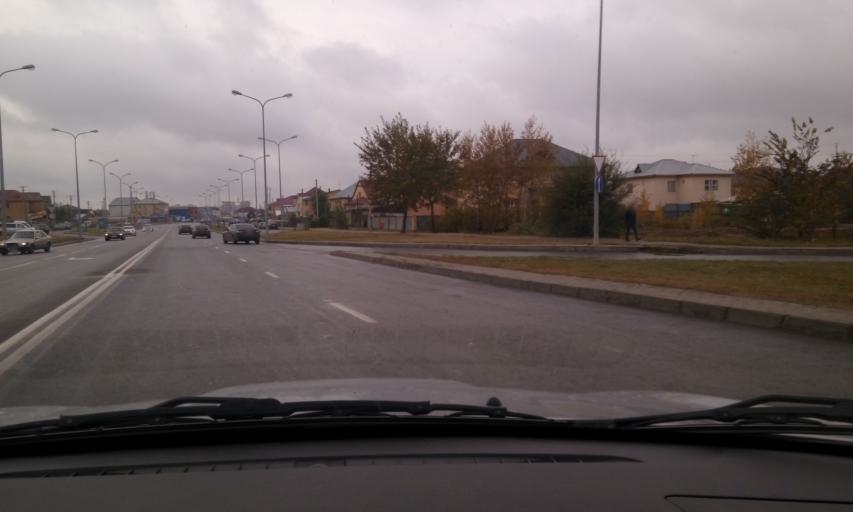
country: KZ
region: Astana Qalasy
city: Astana
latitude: 51.1407
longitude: 71.5216
